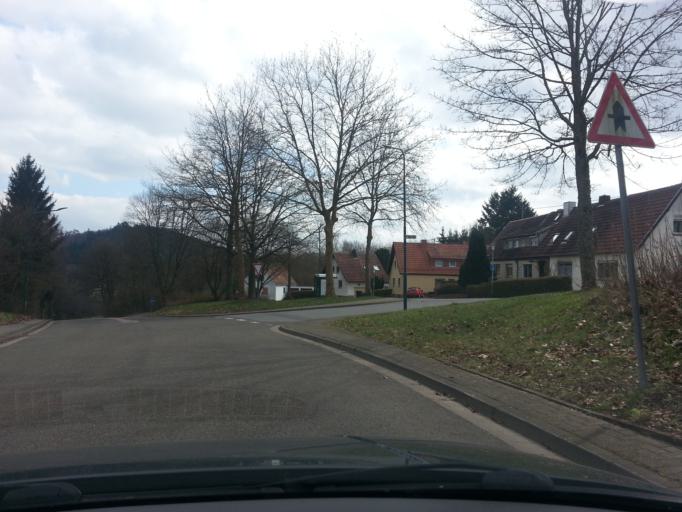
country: DE
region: Saarland
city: Bexbach
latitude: 49.3425
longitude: 7.2220
